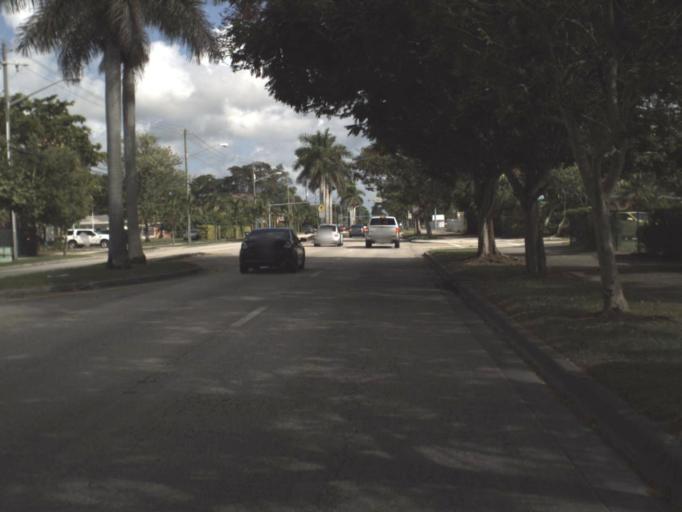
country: US
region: Florida
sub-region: Miami-Dade County
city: Leisure City
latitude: 25.4993
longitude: -80.4415
